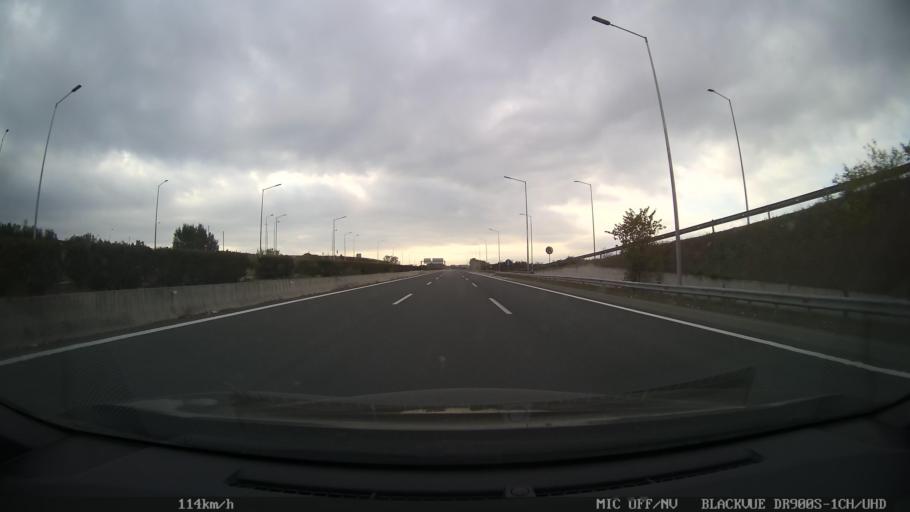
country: GR
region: Central Macedonia
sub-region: Nomos Pierias
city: Nea Efesos
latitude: 40.1932
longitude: 22.5492
